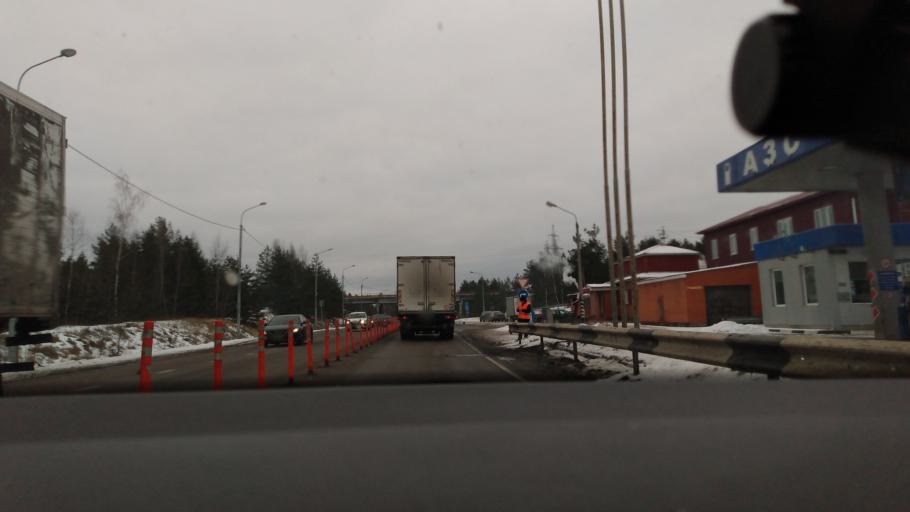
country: RU
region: Moskovskaya
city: Yegor'yevsk
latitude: 55.4170
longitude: 39.0440
